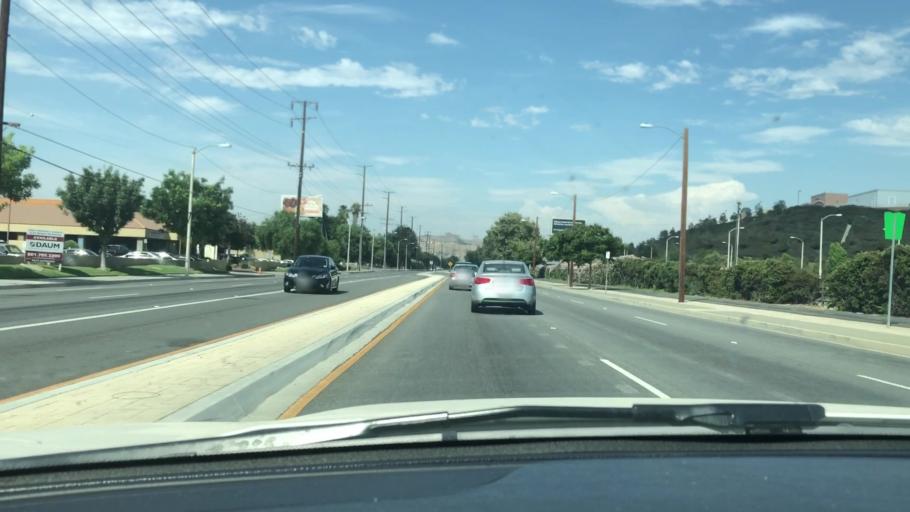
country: US
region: California
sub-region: Los Angeles County
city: Santa Clarita
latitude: 34.4165
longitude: -118.5126
